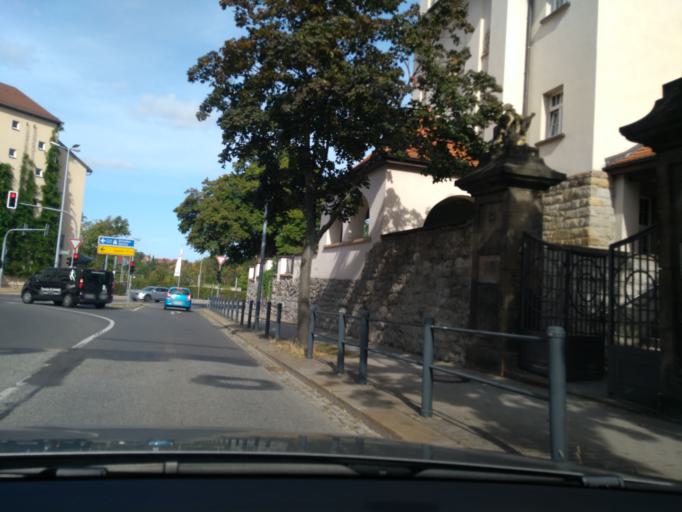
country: DE
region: Saxony
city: Bautzen
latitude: 51.1759
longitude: 14.4244
